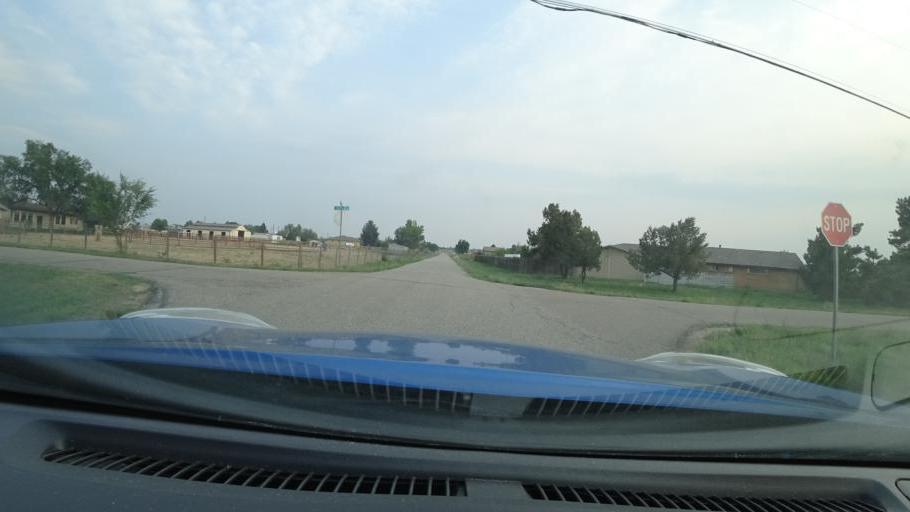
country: US
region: Colorado
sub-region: Adams County
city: Aurora
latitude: 39.7366
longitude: -104.7889
